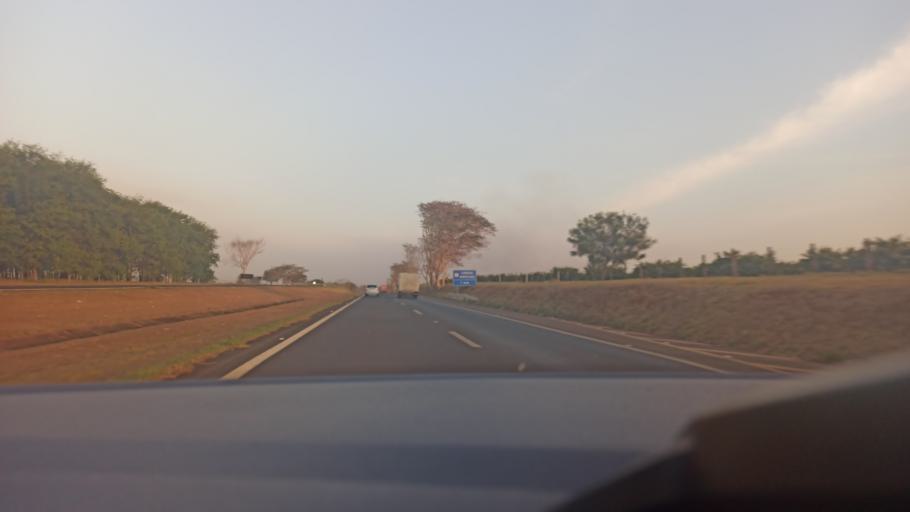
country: BR
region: Sao Paulo
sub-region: Taquaritinga
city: Taquaritinga
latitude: -21.4572
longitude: -48.6254
